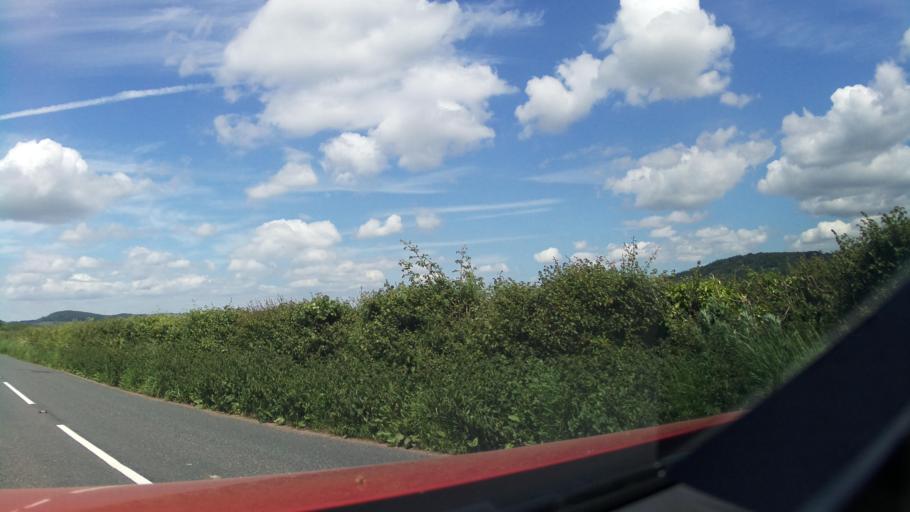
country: GB
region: Wales
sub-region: Monmouthshire
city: Monmouth
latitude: 51.7929
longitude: -2.7165
